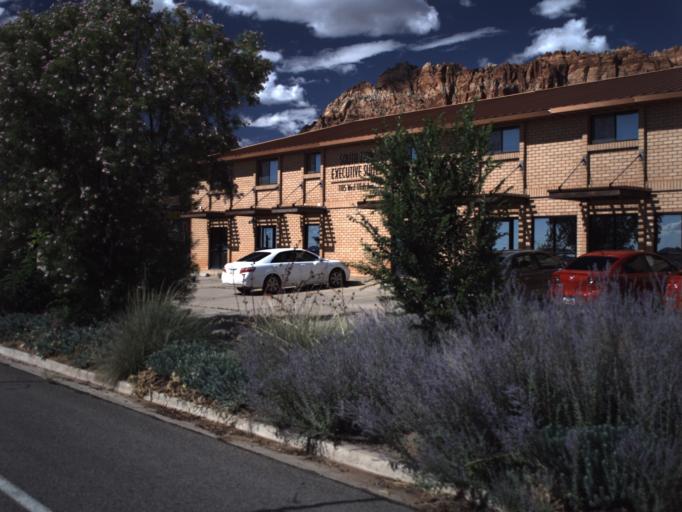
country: US
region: Arizona
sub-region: Mohave County
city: Colorado City
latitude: 37.0026
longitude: -113.0010
